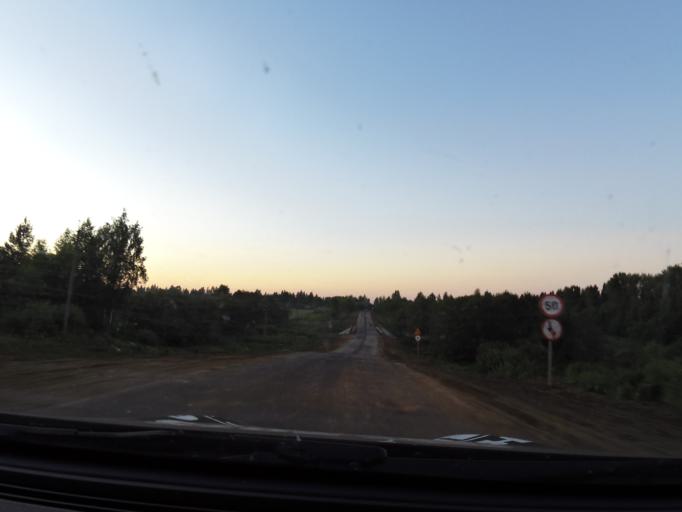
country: RU
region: Kostroma
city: Buy
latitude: 58.4467
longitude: 41.3516
